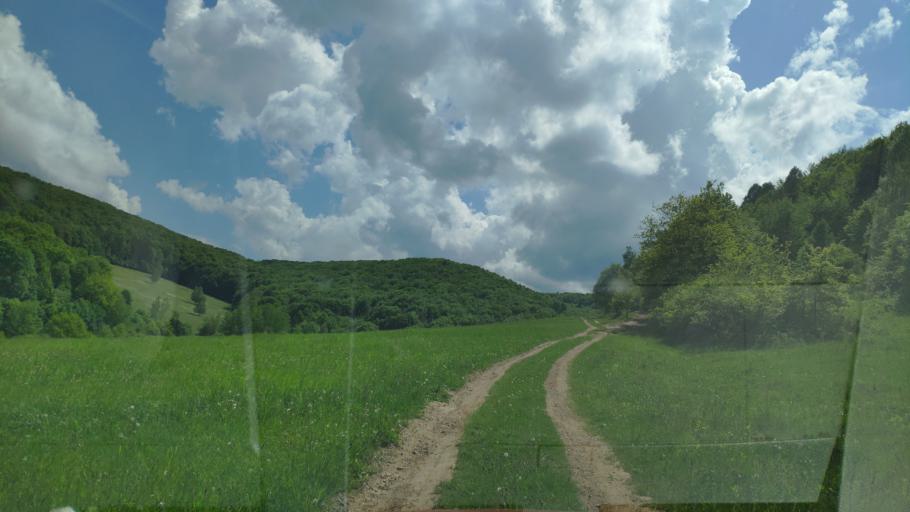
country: SK
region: Presovsky
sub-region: Okres Presov
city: Presov
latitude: 48.9487
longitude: 21.1145
